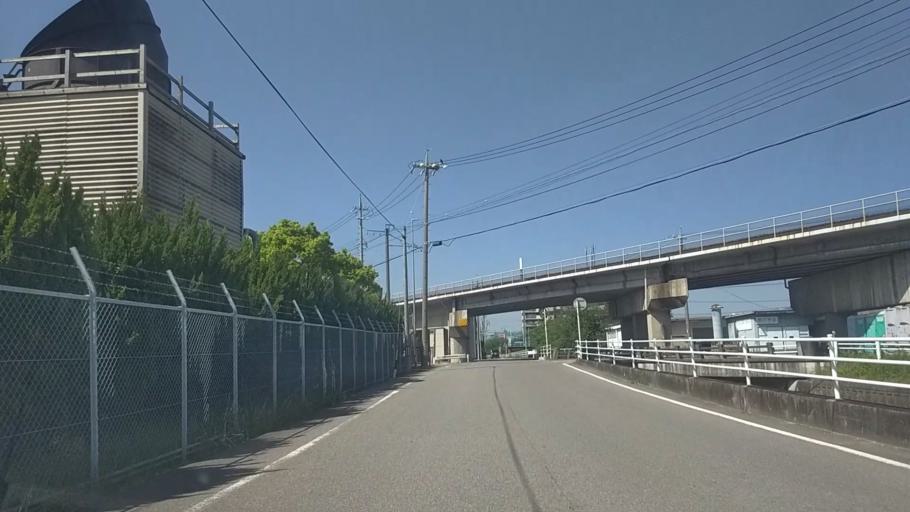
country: JP
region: Aichi
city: Okazaki
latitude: 34.9780
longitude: 137.1572
